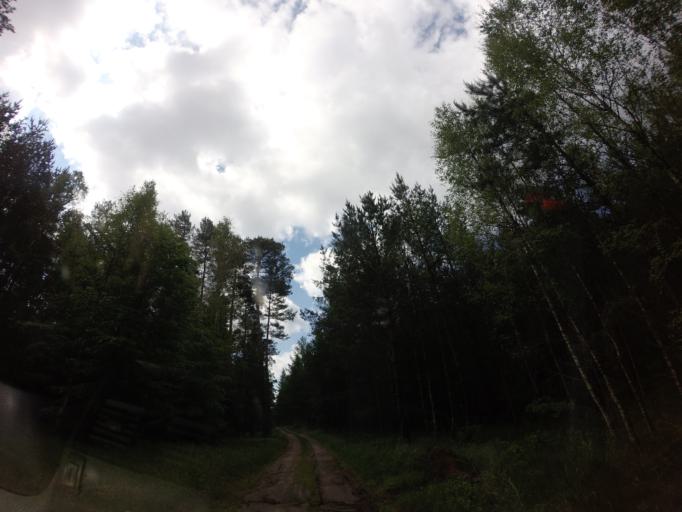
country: PL
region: West Pomeranian Voivodeship
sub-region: Powiat choszczenski
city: Drawno
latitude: 53.2020
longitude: 15.6984
